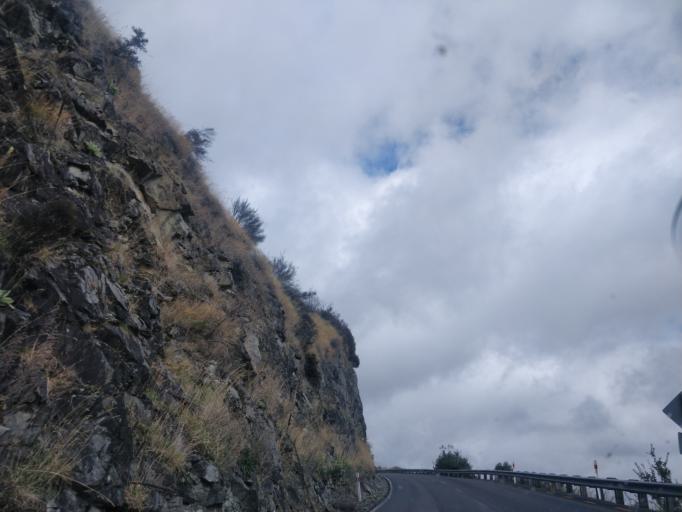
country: NZ
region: Canterbury
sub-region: Waimakariri District
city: Oxford
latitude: -43.0173
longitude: 171.7071
